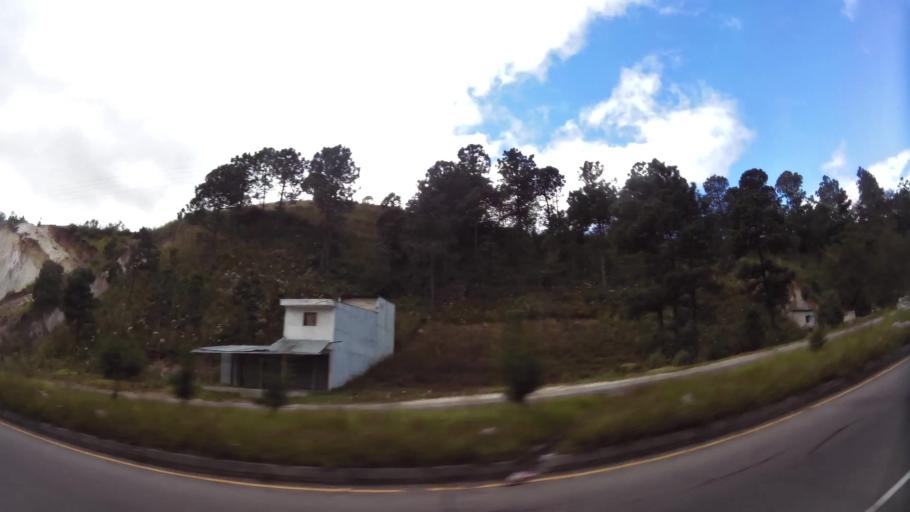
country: GT
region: Quetzaltenango
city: Salcaja
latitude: 14.8717
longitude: -91.4706
